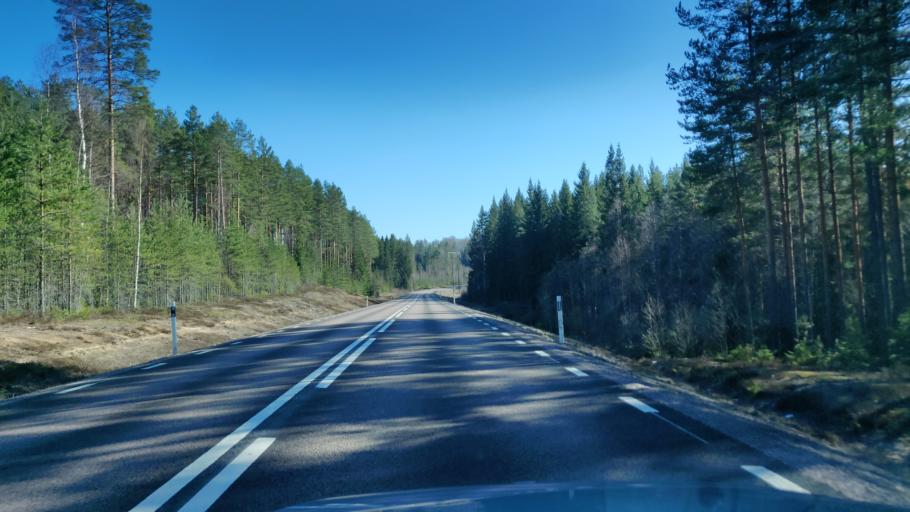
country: SE
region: Vaermland
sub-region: Hagfors Kommun
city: Hagfors
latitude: 59.9274
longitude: 13.6747
